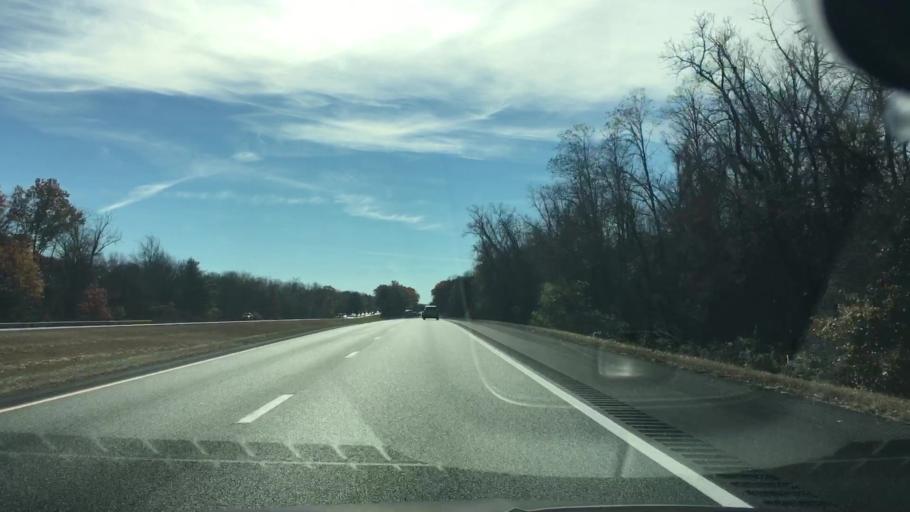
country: US
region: Massachusetts
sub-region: Franklin County
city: Whately
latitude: 42.4089
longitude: -72.6267
